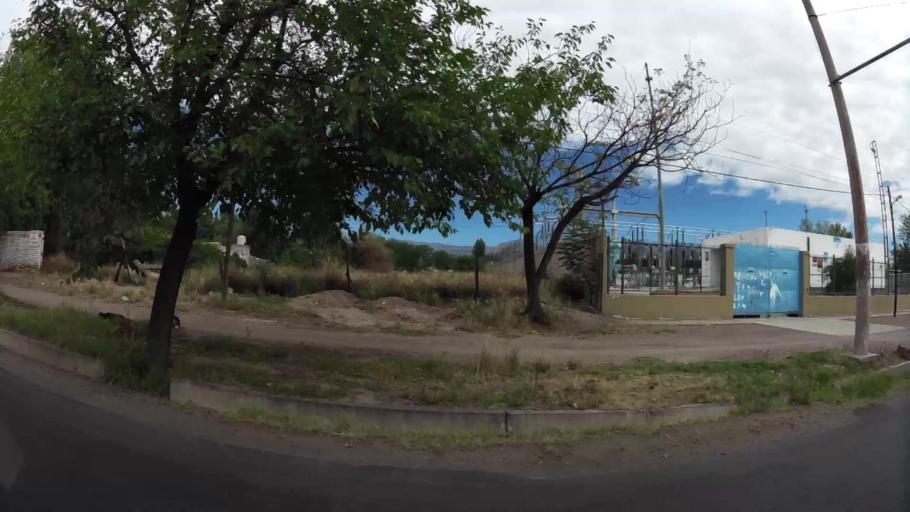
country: AR
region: Mendoza
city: Las Heras
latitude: -32.8624
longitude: -68.8587
